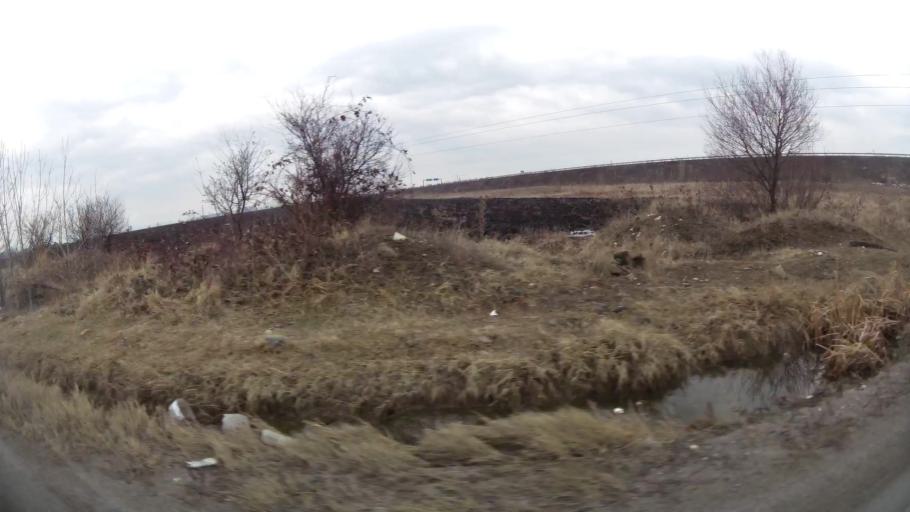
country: BG
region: Sofiya
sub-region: Obshtina Bozhurishte
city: Bozhurishte
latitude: 42.7110
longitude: 23.2194
